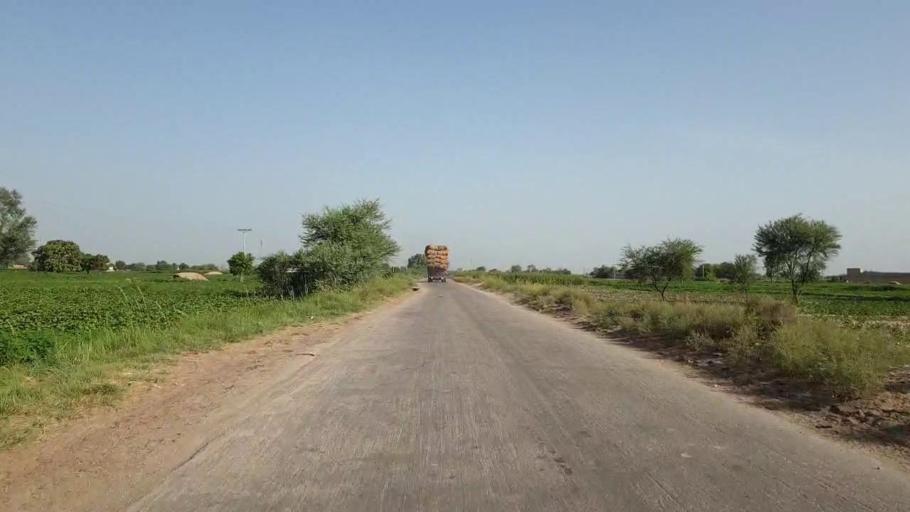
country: PK
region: Sindh
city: Nawabshah
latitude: 26.0969
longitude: 68.4695
